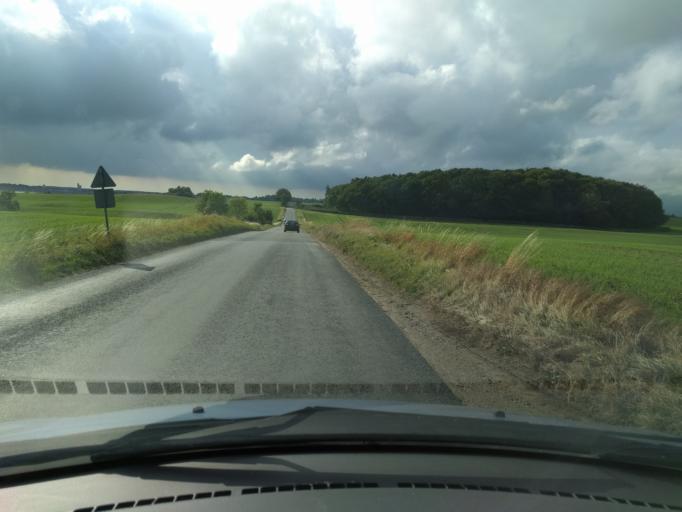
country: DK
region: South Denmark
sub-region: Kerteminde Kommune
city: Kerteminde
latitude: 55.4714
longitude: 10.6931
